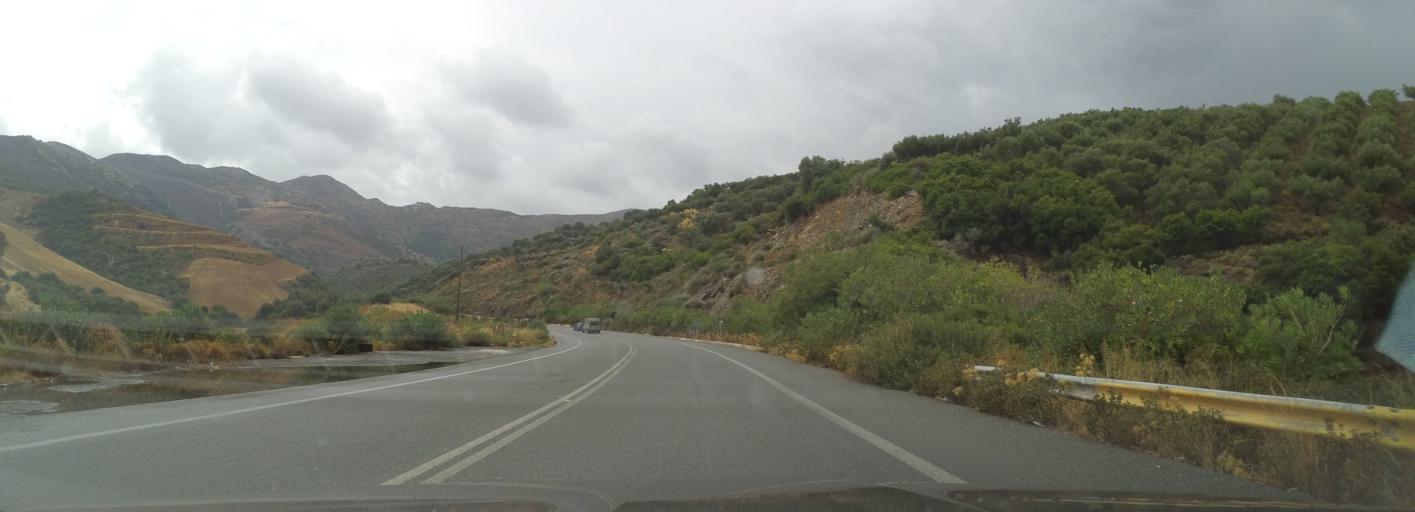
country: GR
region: Crete
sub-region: Nomos Rethymnis
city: Anogeia
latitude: 35.3921
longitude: 24.9210
